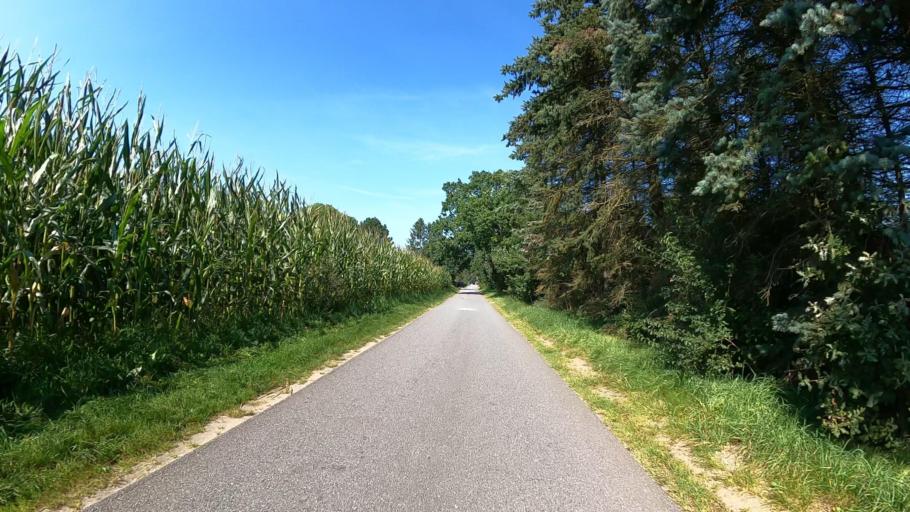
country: DE
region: Schleswig-Holstein
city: Nutzen
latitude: 53.8601
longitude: 9.9200
